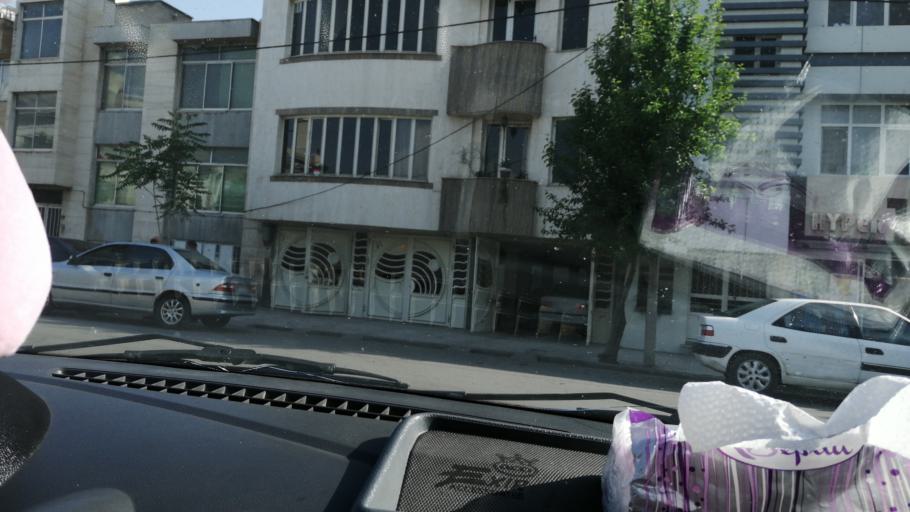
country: IR
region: Razavi Khorasan
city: Mashhad
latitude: 36.3117
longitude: 59.5611
